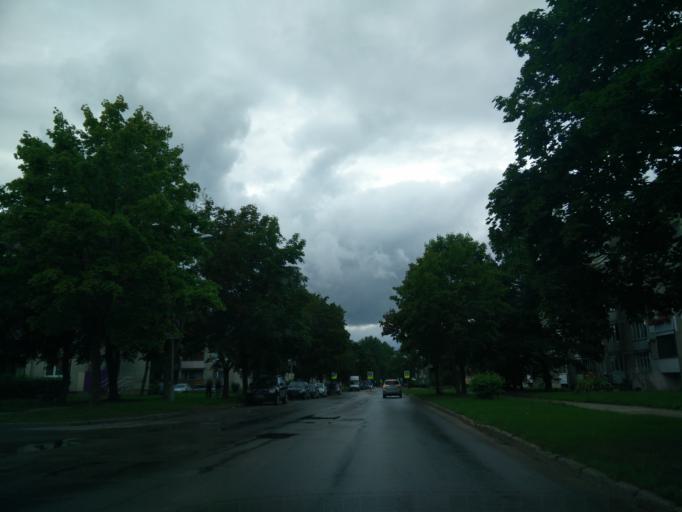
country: LT
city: Grigiskes
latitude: 54.6699
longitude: 25.0951
